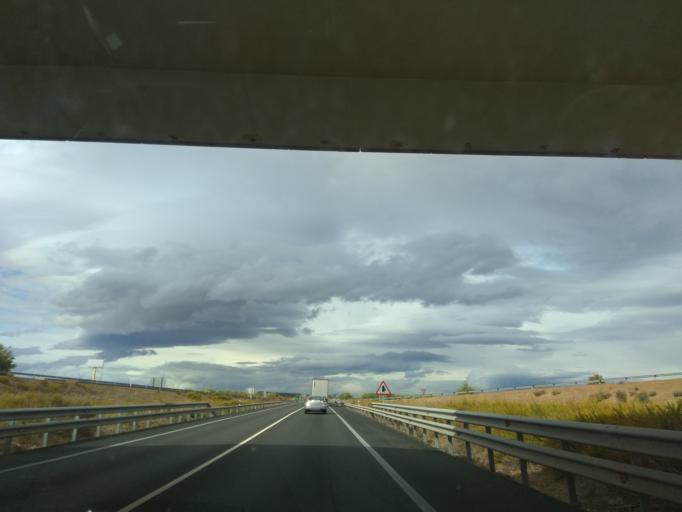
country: ES
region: La Rioja
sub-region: Provincia de La Rioja
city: Aldeanueva de Ebro
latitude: 42.2503
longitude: -1.8971
